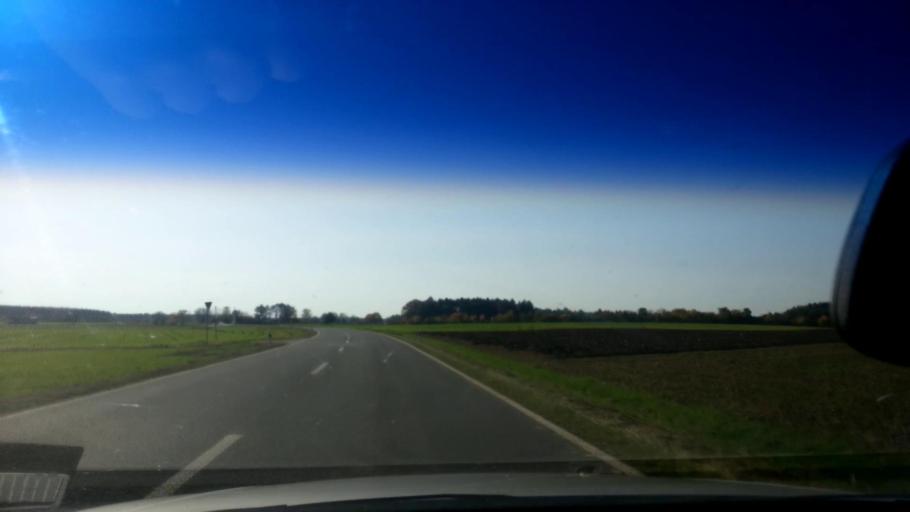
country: DE
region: Bavaria
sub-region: Upper Franconia
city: Wonsees
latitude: 49.9690
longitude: 11.2633
